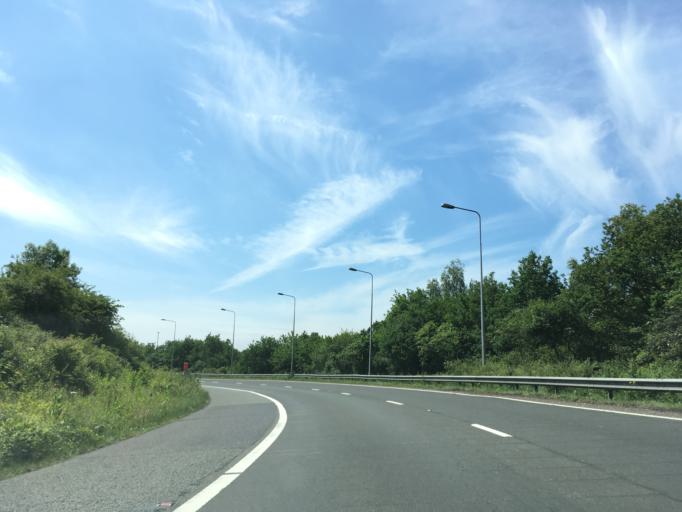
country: GB
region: England
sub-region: Buckinghamshire
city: Gerrards Cross
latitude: 51.5633
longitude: -0.5361
